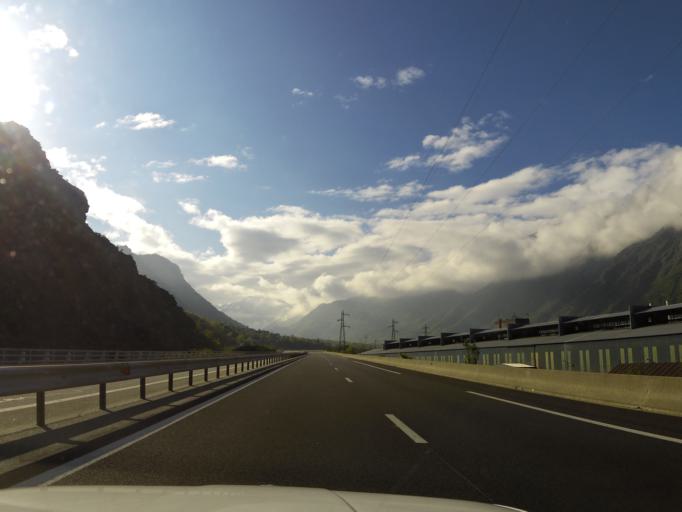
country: FR
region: Rhone-Alpes
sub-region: Departement de la Savoie
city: Villargondran
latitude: 45.2705
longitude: 6.3777
